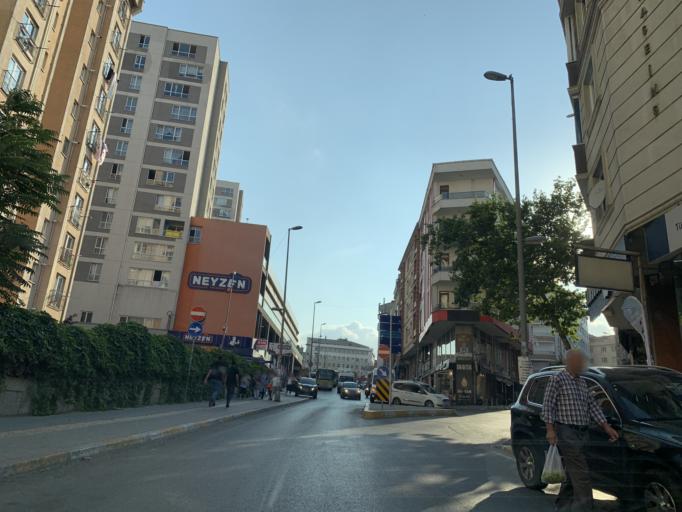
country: TR
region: Istanbul
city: Esenyurt
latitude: 41.0425
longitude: 28.6788
